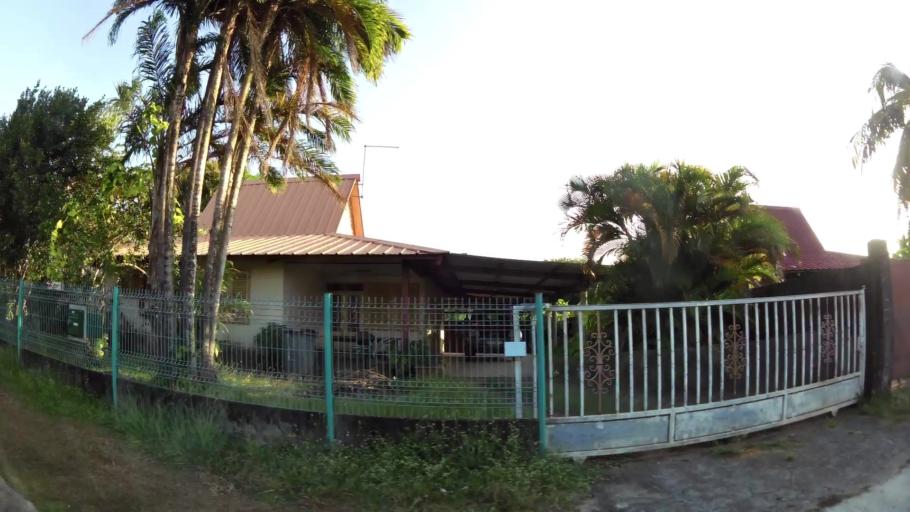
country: GF
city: Macouria
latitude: 5.0159
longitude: -52.4796
